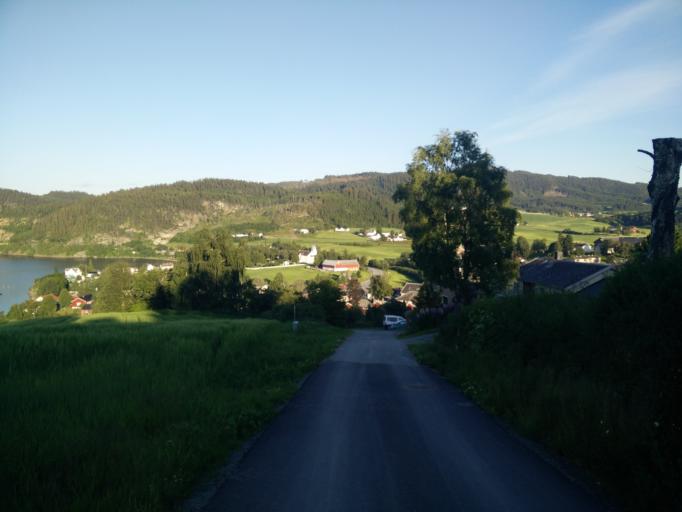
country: NO
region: Sor-Trondelag
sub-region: Skaun
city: Borsa
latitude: 63.3291
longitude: 10.0648
